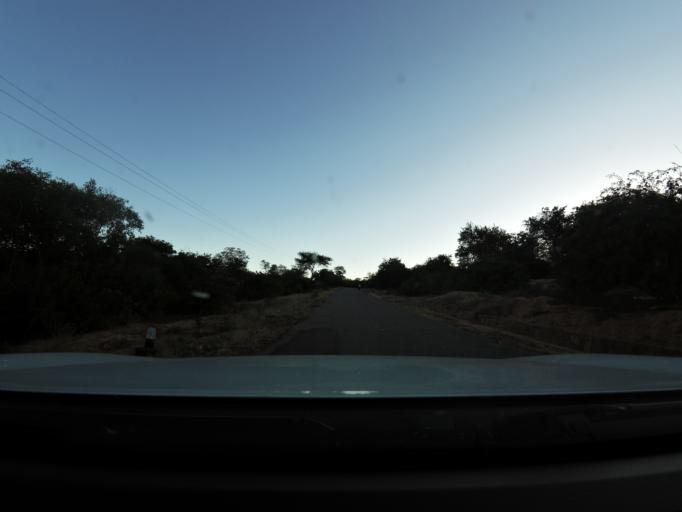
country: ZW
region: Matabeleland North
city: Binga
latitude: -17.6257
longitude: 27.3559
